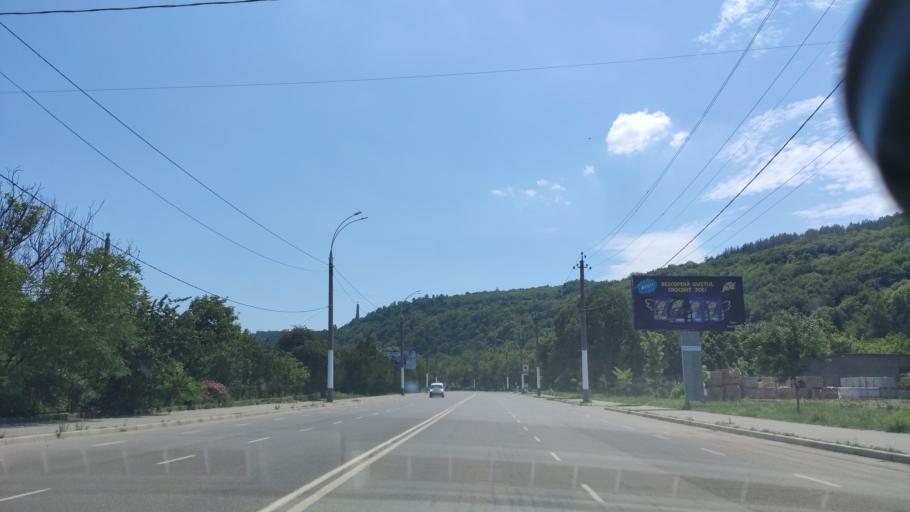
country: MD
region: Raionul Soroca
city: Soroca
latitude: 48.1459
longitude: 28.3021
